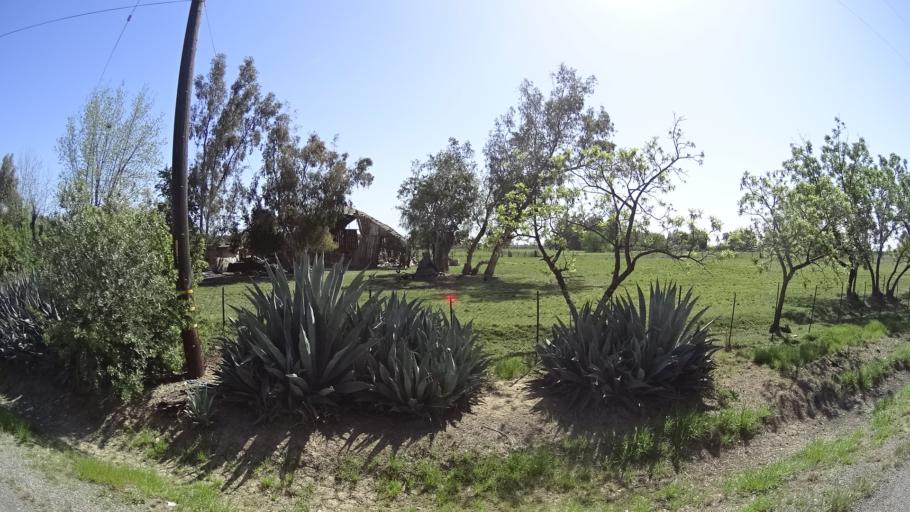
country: US
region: California
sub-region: Glenn County
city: Orland
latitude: 39.7210
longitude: -122.1924
